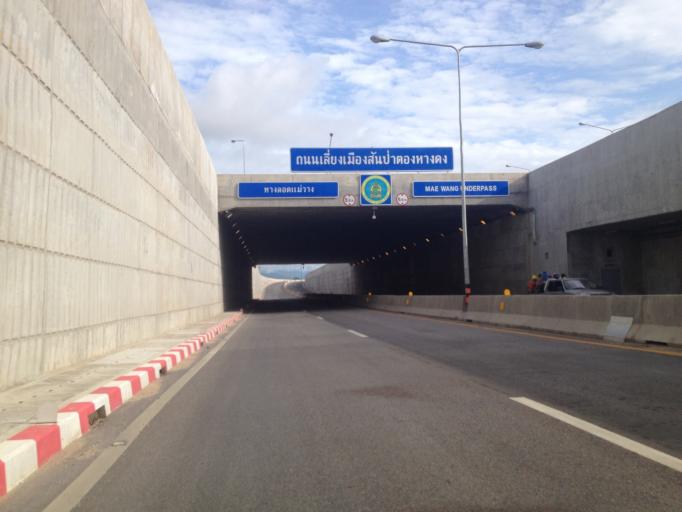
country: TH
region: Chiang Mai
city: Mae Wang
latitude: 18.6049
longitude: 98.8348
